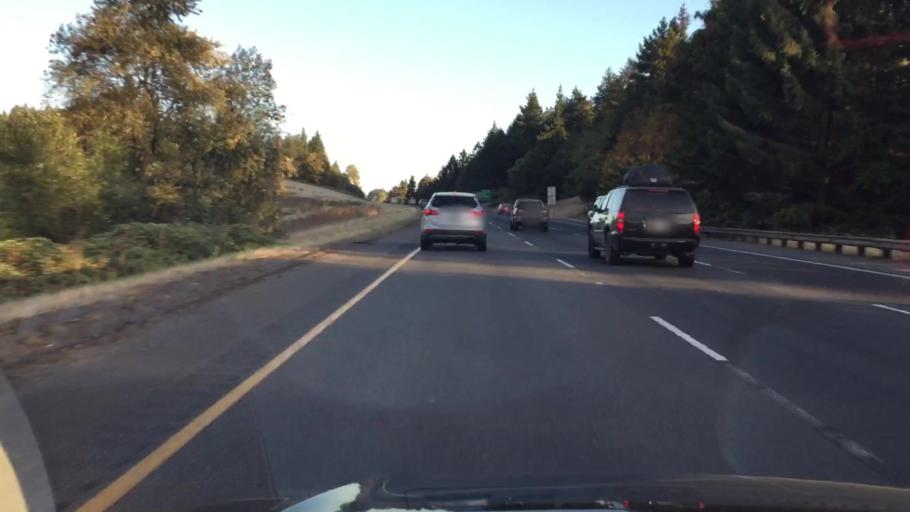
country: US
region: Washington
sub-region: Cowlitz County
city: Kalama
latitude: 45.9979
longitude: -122.8417
